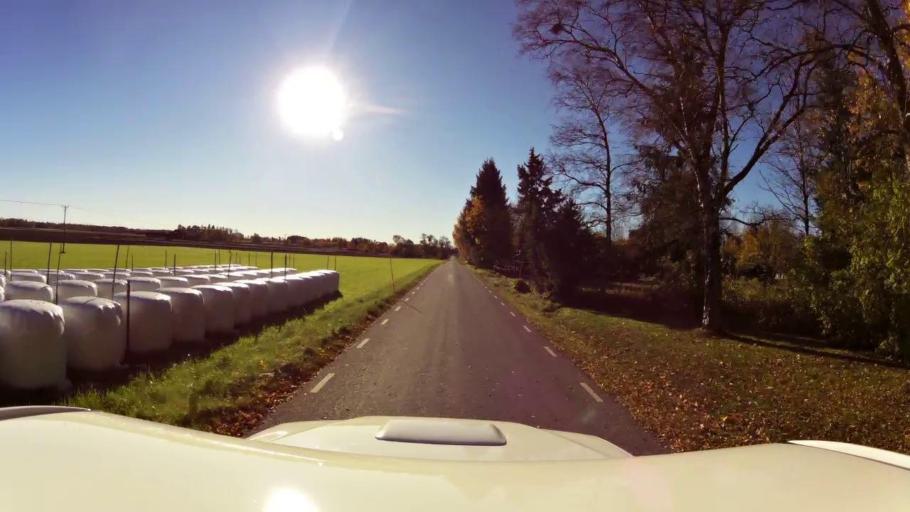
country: SE
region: OEstergoetland
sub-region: Linkopings Kommun
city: Ljungsbro
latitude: 58.5004
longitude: 15.4187
